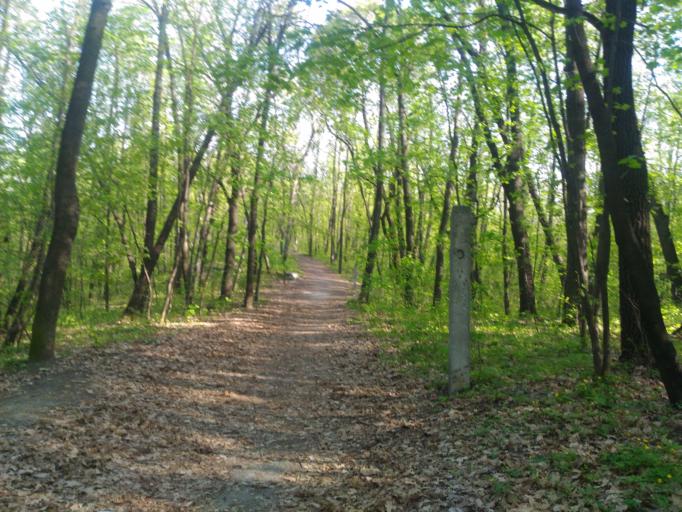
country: RU
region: Ulyanovsk
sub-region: Ulyanovskiy Rayon
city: Ulyanovsk
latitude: 54.2736
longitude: 48.3405
